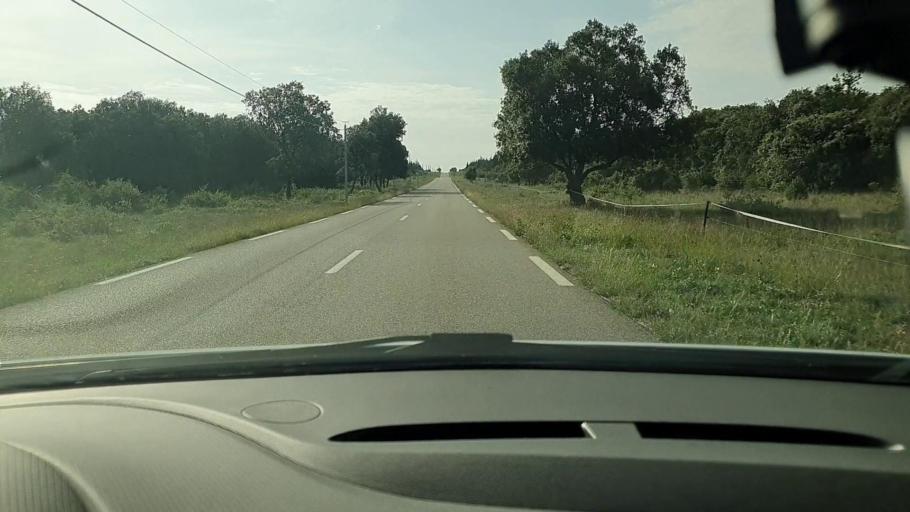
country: FR
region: Languedoc-Roussillon
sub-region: Departement du Gard
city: Montaren-et-Saint-Mediers
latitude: 44.0776
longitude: 4.3930
